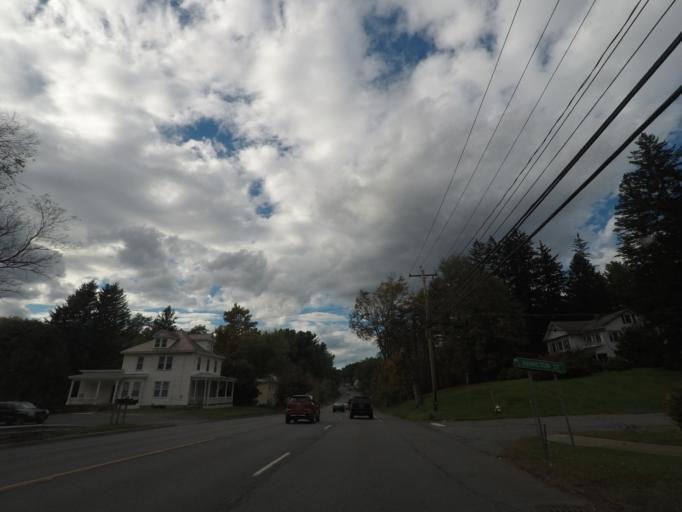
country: US
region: New York
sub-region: Albany County
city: Westmere
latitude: 42.7046
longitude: -73.9122
